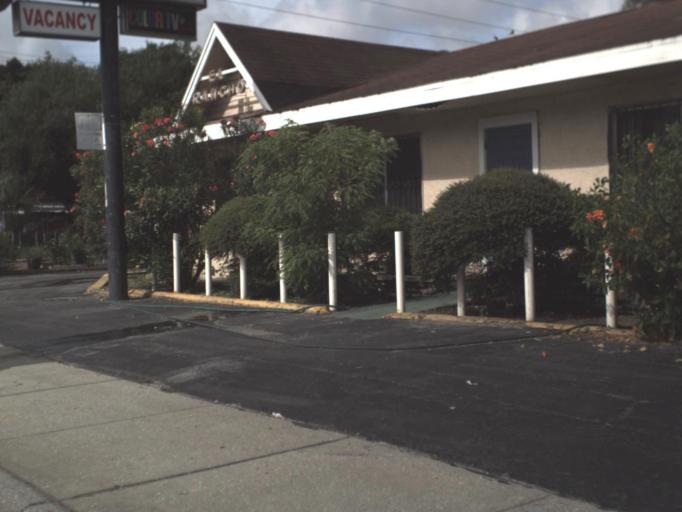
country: US
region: Florida
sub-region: Hillsborough County
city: Egypt Lake-Leto
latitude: 28.0128
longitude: -82.4513
